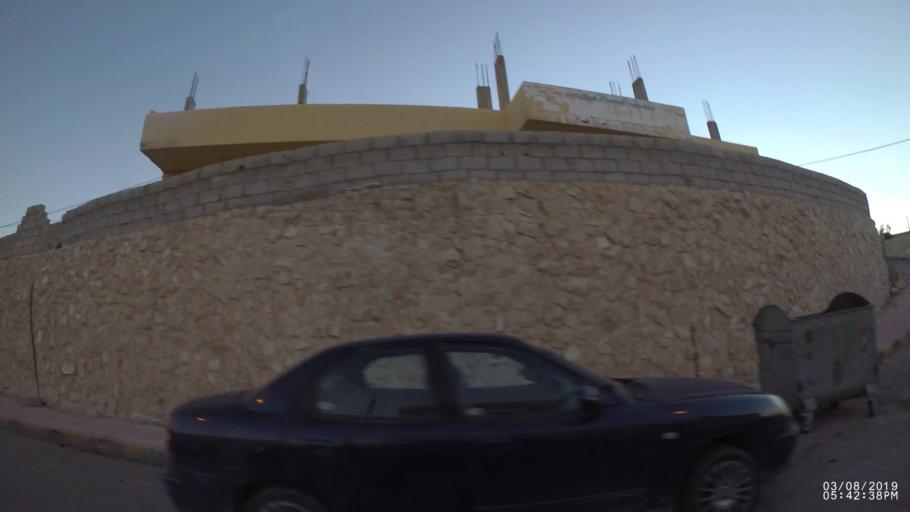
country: JO
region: Ma'an
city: Petra
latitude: 30.3169
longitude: 35.4755
